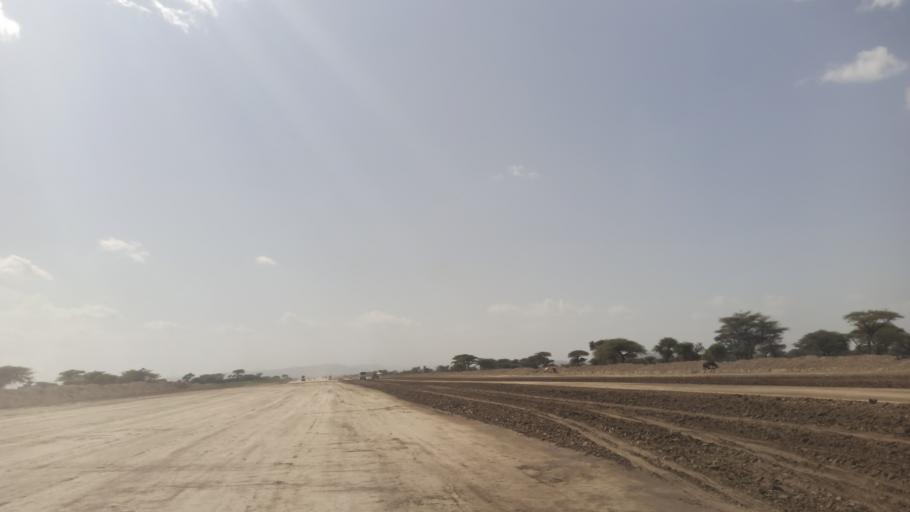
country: ET
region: Oromiya
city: Ziway
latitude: 7.7129
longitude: 38.6349
